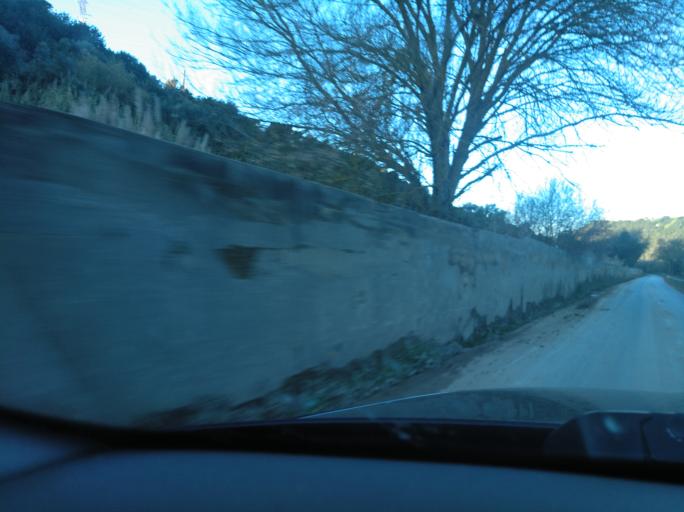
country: PT
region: Lisbon
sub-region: Loures
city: Bobadela
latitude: 38.8063
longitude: -9.1089
